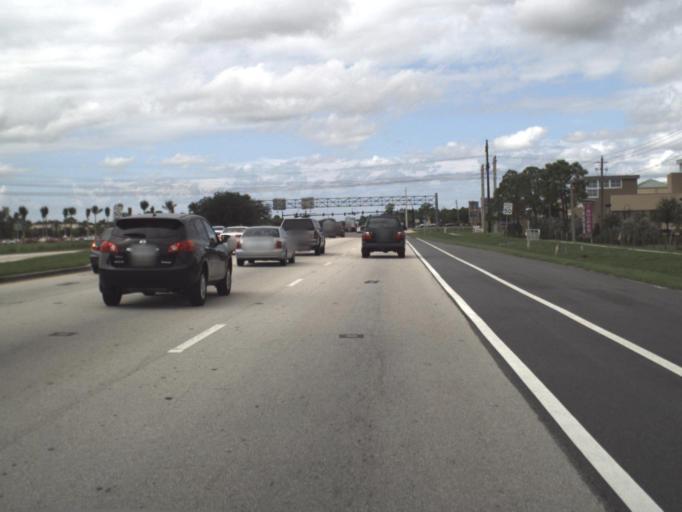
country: US
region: Florida
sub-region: Sarasota County
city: The Meadows
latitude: 27.3888
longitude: -82.4519
